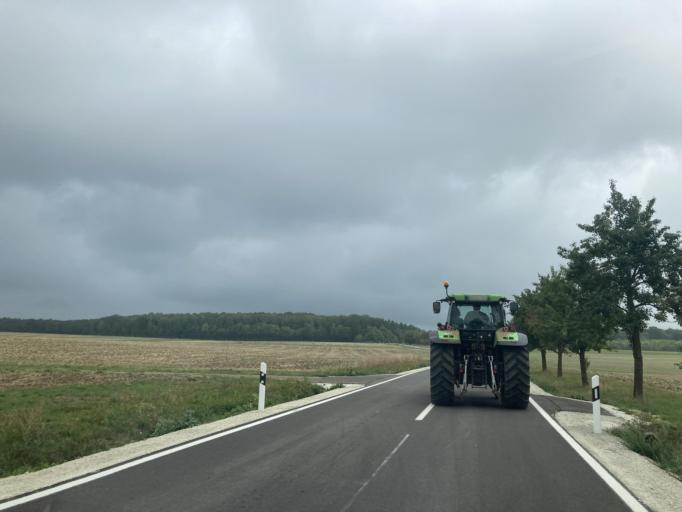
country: DE
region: Bavaria
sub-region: Swabia
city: Forheim
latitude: 48.7894
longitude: 10.4157
